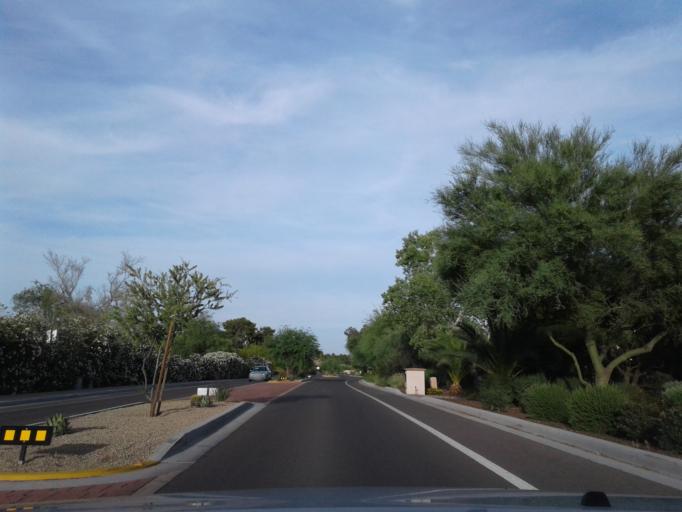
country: US
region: Arizona
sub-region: Maricopa County
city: Paradise Valley
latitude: 33.5608
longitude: -111.9645
